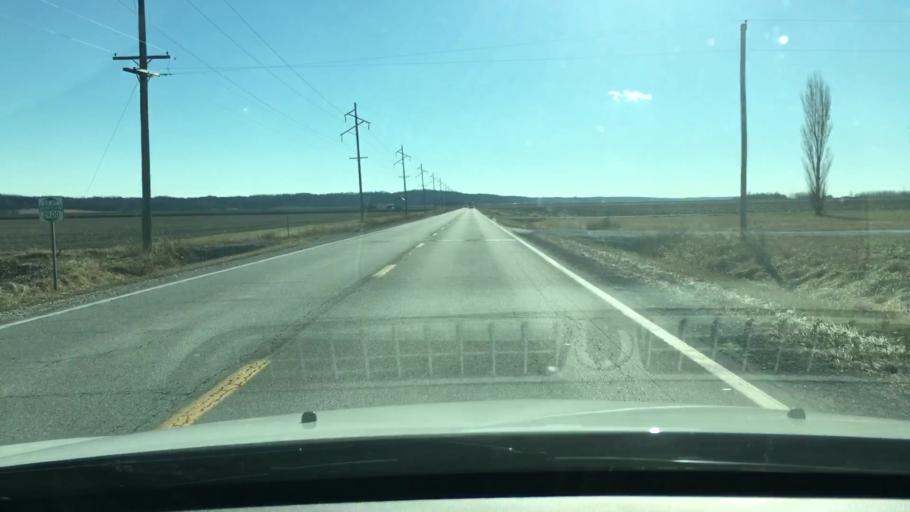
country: US
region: Illinois
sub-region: Morgan County
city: Meredosia
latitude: 39.8620
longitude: -90.5054
